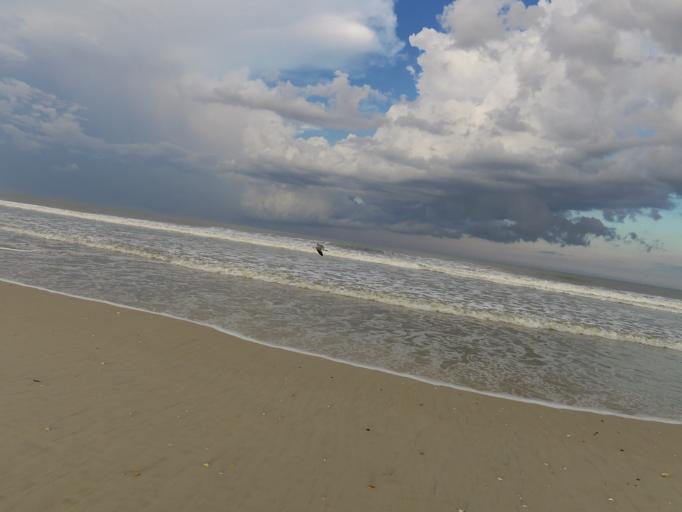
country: US
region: Florida
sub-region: Saint Johns County
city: Villano Beach
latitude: 29.9692
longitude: -81.3090
